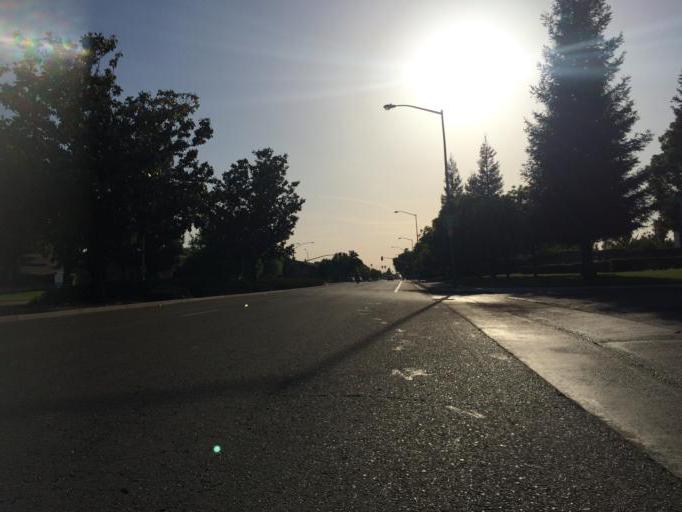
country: US
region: California
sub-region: Fresno County
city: Tarpey Village
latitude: 36.7723
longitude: -119.7299
